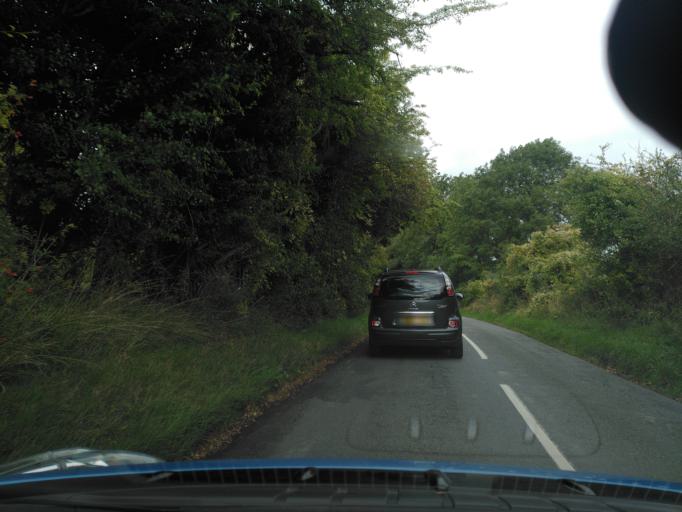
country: GB
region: England
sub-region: Oxfordshire
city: Stanford in the Vale
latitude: 51.5827
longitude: -1.5486
